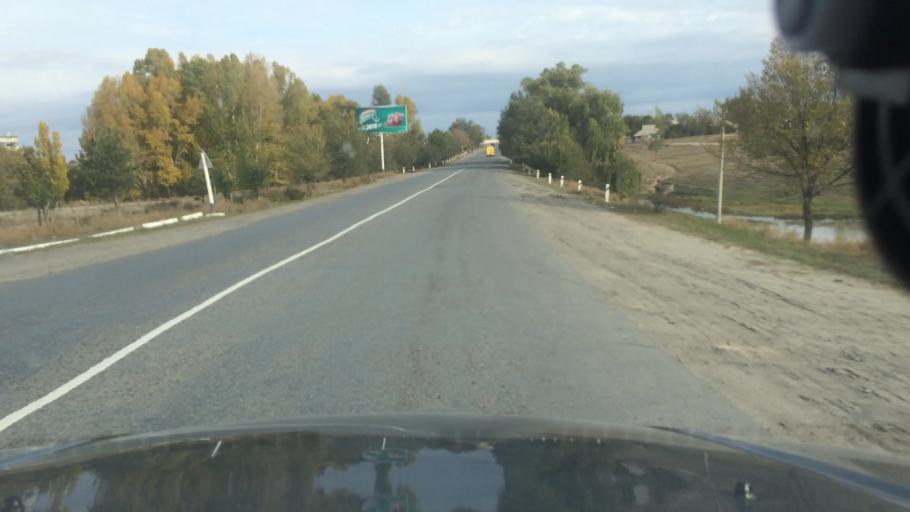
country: KG
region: Ysyk-Koel
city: Karakol
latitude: 42.5327
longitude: 78.3816
